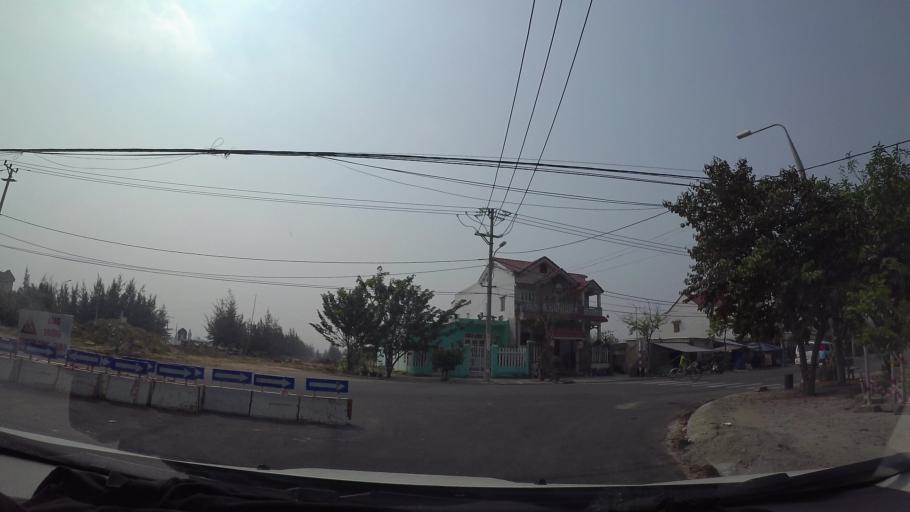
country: VN
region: Da Nang
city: Ngu Hanh Son
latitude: 15.9906
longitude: 108.2463
